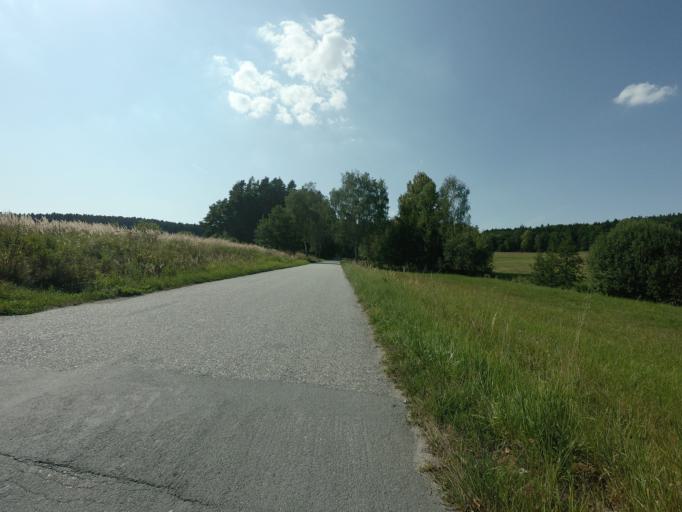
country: CZ
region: Jihocesky
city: Tyn nad Vltavou
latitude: 49.1551
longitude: 14.4390
